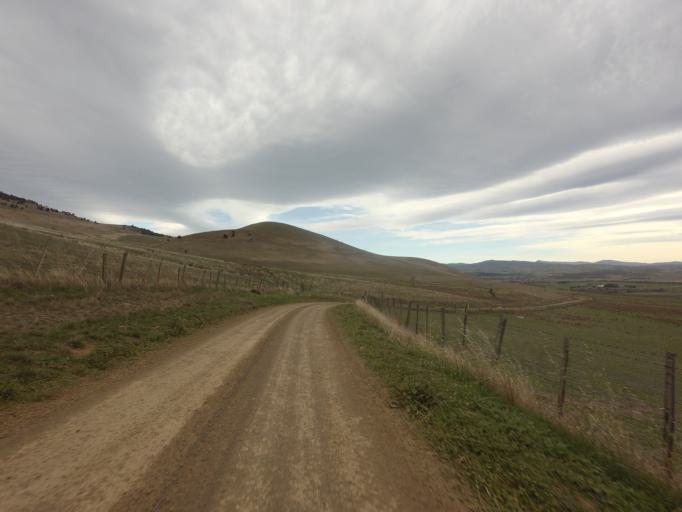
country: AU
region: Tasmania
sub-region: Derwent Valley
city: New Norfolk
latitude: -42.4585
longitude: 146.7613
